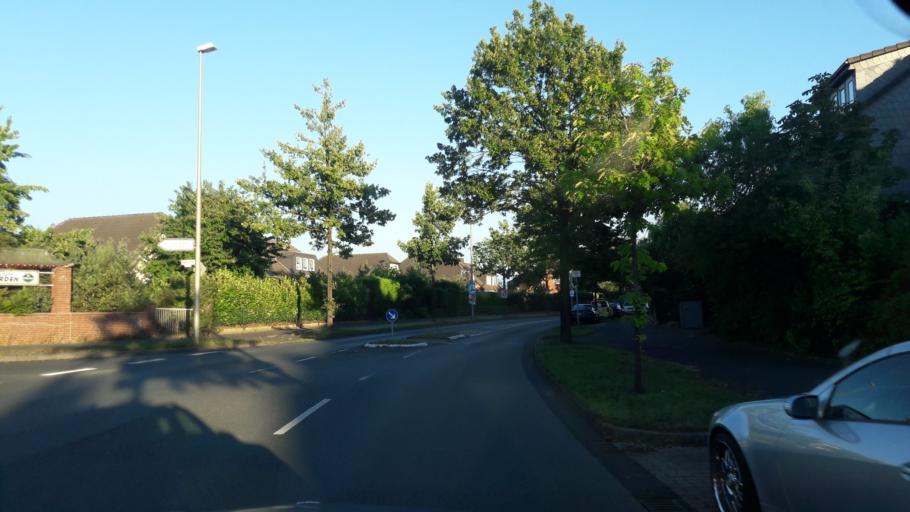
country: DE
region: Lower Saxony
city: Hildesheim
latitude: 52.1221
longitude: 9.9837
